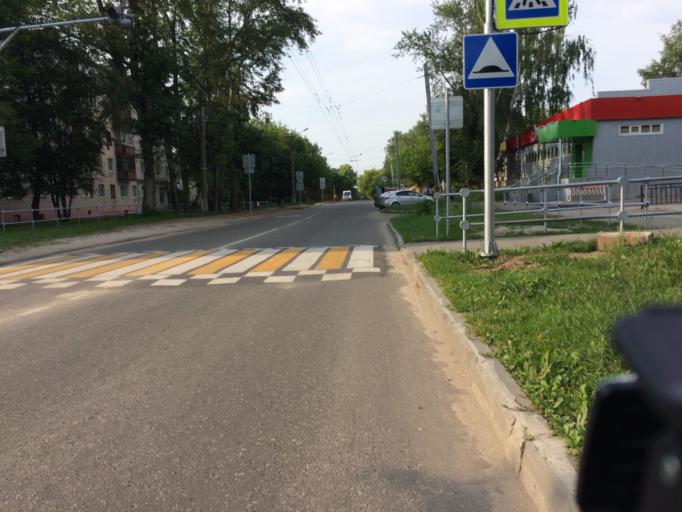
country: RU
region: Mariy-El
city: Yoshkar-Ola
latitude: 56.6245
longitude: 47.9462
